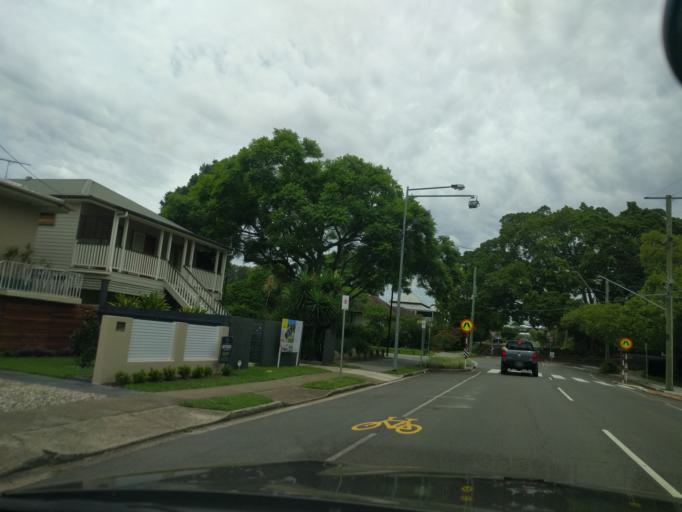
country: AU
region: Queensland
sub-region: Brisbane
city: Milton
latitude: -27.4679
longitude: 152.9995
